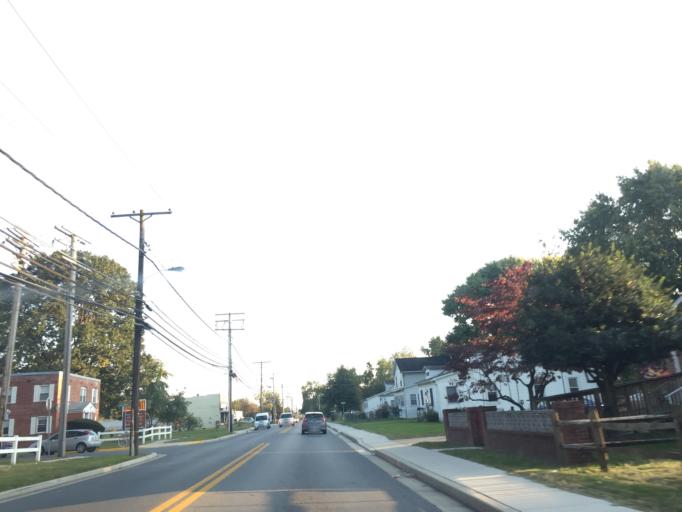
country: US
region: Maryland
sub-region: Baltimore County
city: Essex
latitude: 39.3096
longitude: -76.4647
